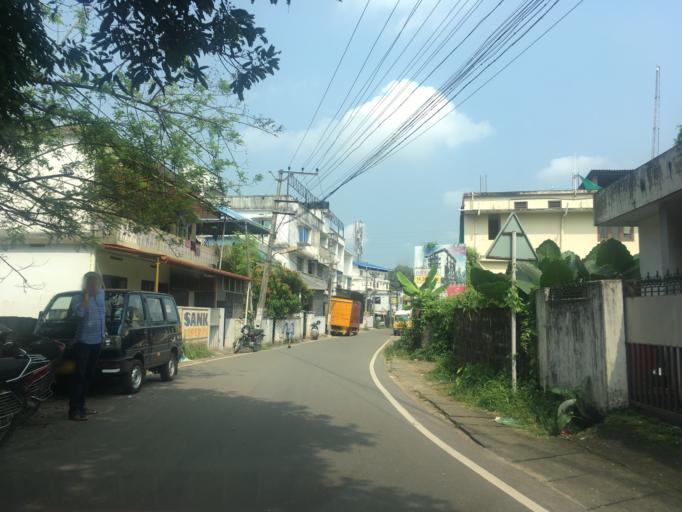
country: IN
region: Kerala
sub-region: Ernakulam
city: Elur
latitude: 10.0413
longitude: 76.3055
